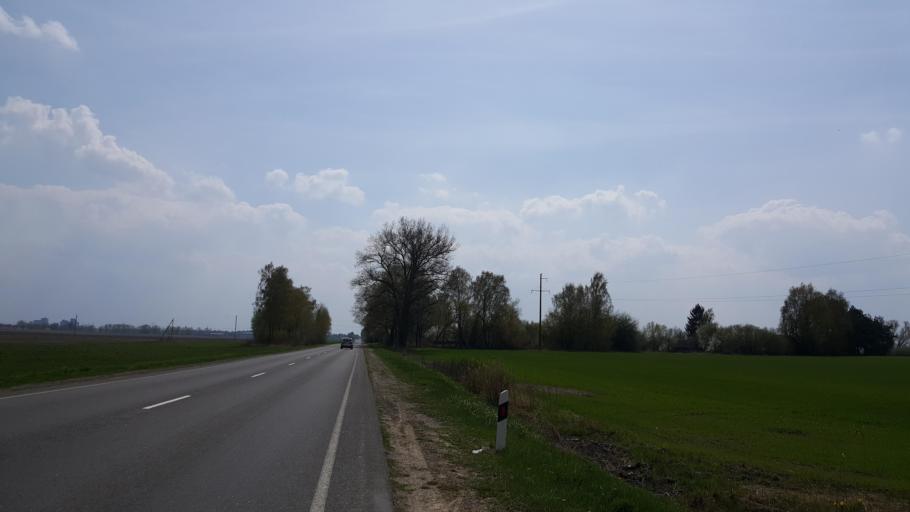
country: BY
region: Brest
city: Zhabinka
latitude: 52.2225
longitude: 23.9912
